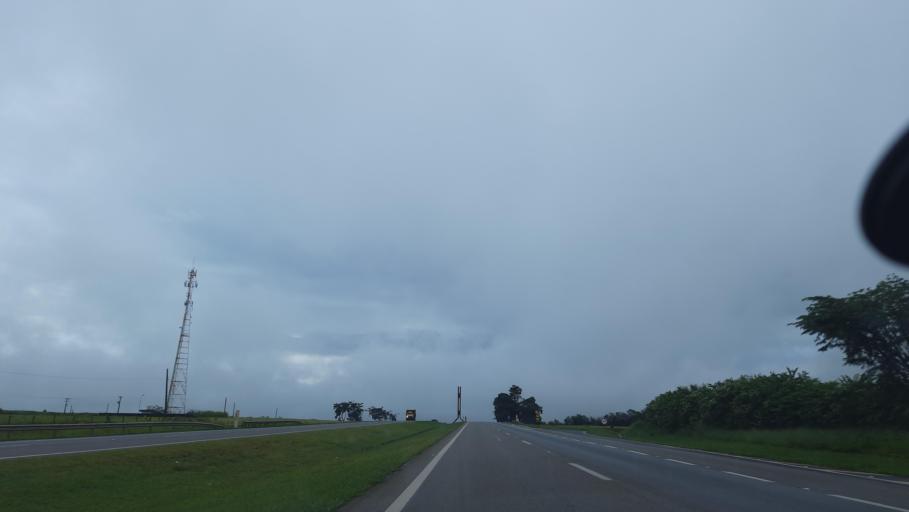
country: BR
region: Sao Paulo
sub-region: Aguai
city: Aguai
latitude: -22.1428
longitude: -46.9968
